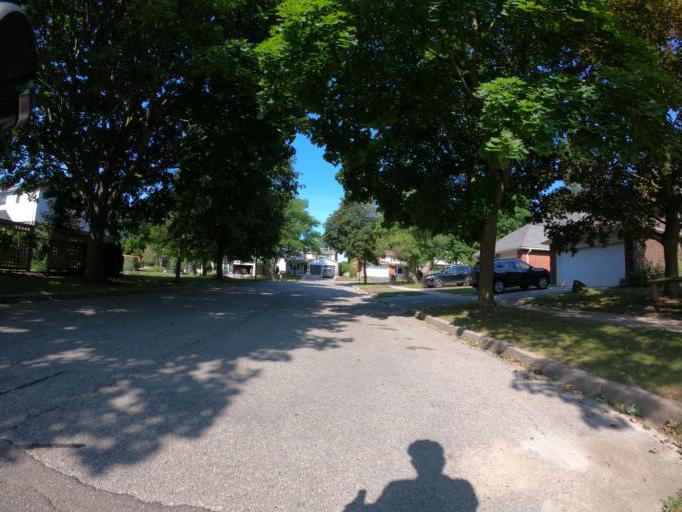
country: CA
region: Ontario
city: Waterloo
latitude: 43.4657
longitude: -80.5599
